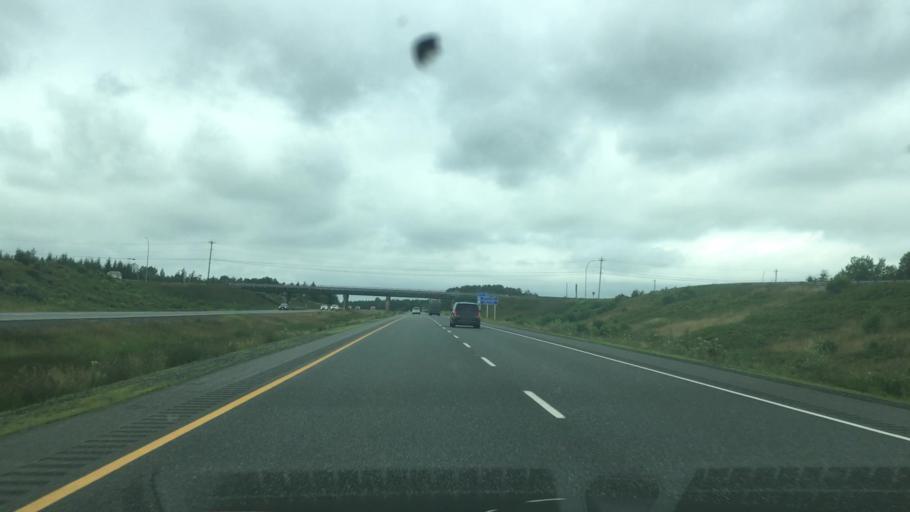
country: CA
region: Nova Scotia
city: Truro
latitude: 45.3970
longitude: -63.4258
